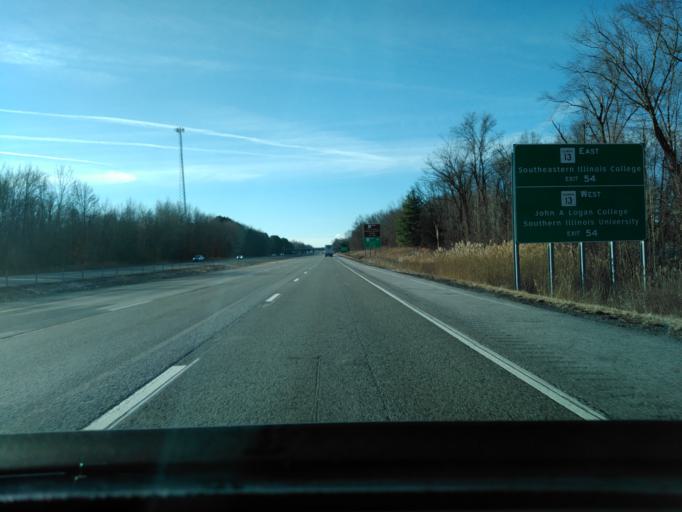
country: US
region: Illinois
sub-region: Williamson County
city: Johnston City
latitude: 37.7989
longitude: -88.9461
